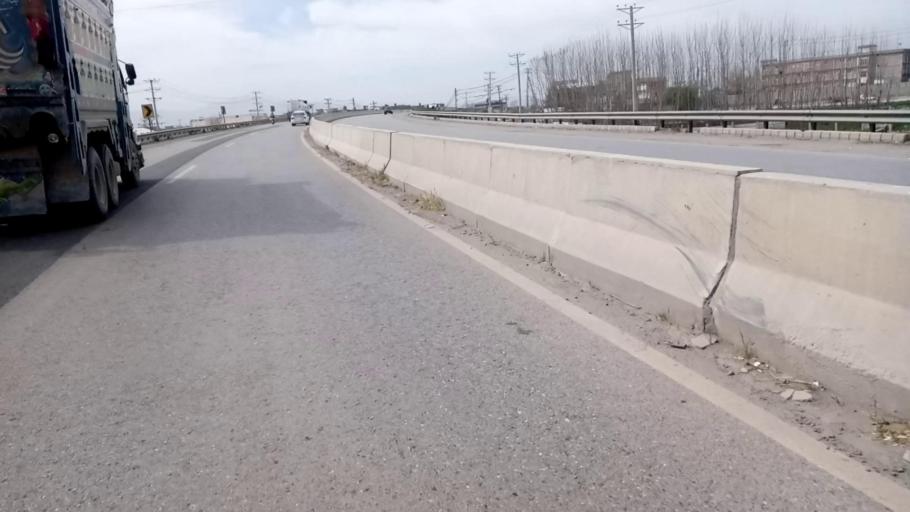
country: PK
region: Khyber Pakhtunkhwa
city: Peshawar
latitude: 34.0380
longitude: 71.6226
